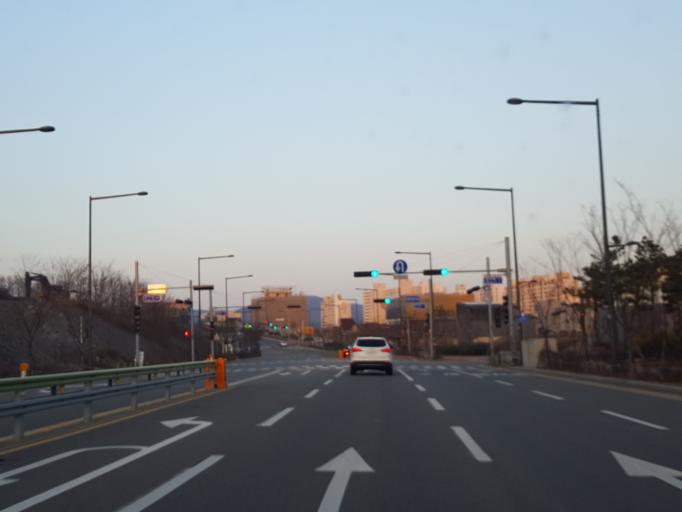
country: KR
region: Ulsan
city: Ulsan
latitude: 35.5663
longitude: 129.3233
